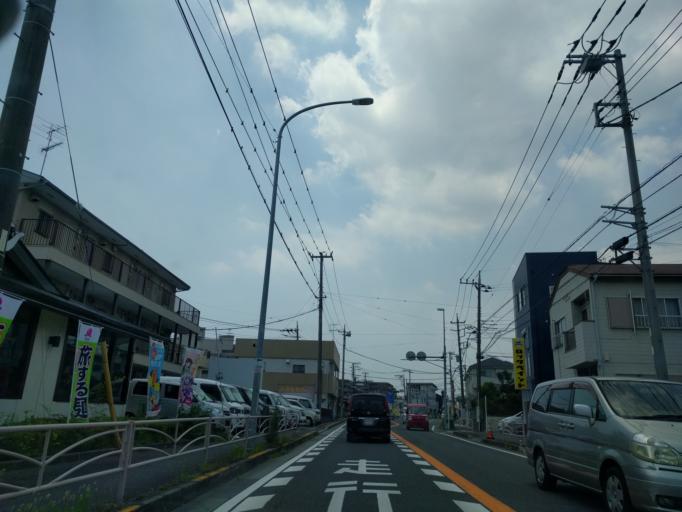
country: JP
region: Kanagawa
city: Minami-rinkan
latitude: 35.4837
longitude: 139.5263
